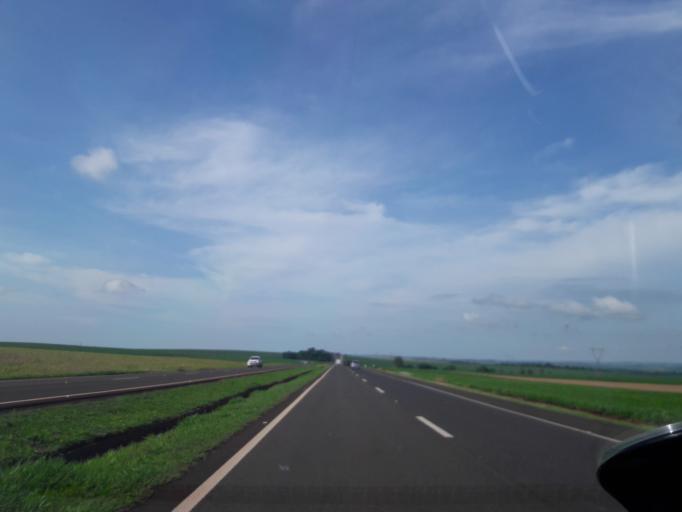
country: BR
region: Parana
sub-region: Paicandu
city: Paicandu
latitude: -23.6222
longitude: -52.0960
